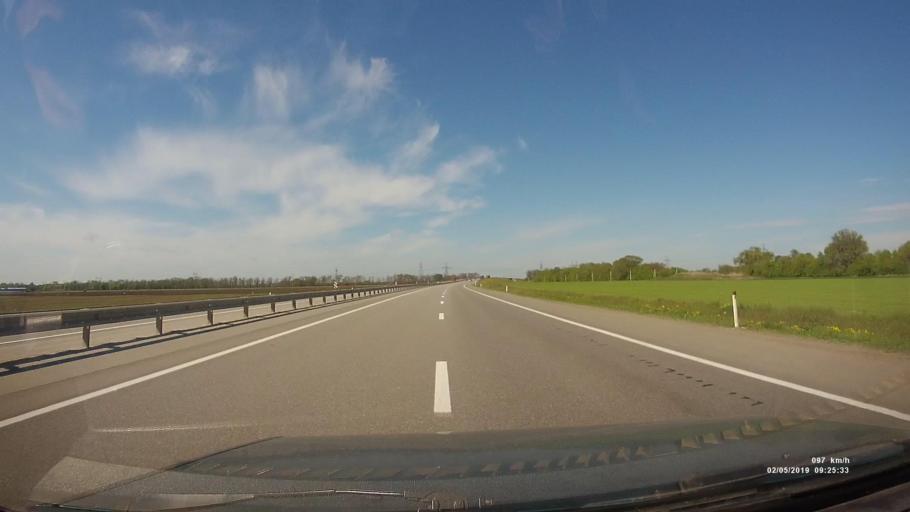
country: RU
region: Rostov
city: Kuleshovka
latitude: 47.1015
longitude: 39.6114
